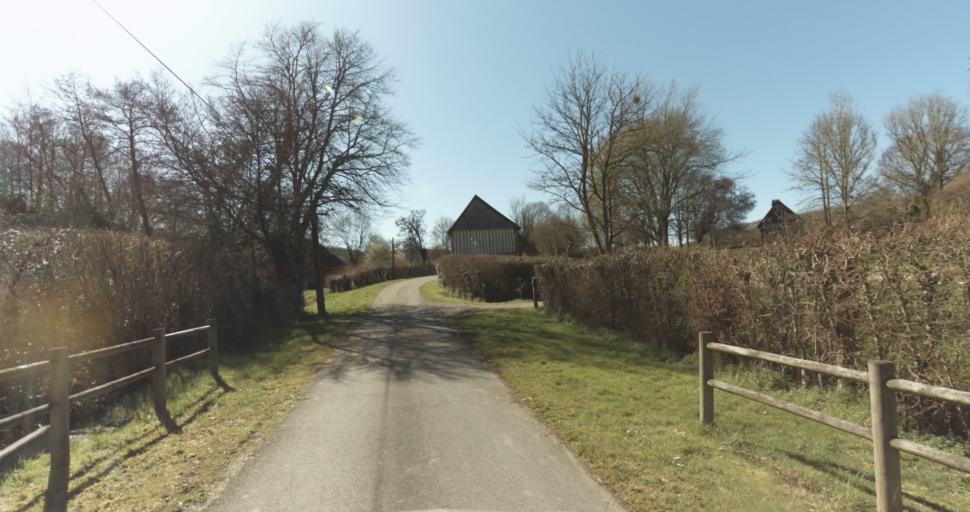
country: FR
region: Lower Normandy
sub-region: Departement du Calvados
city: Livarot
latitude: 48.9483
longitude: 0.0729
